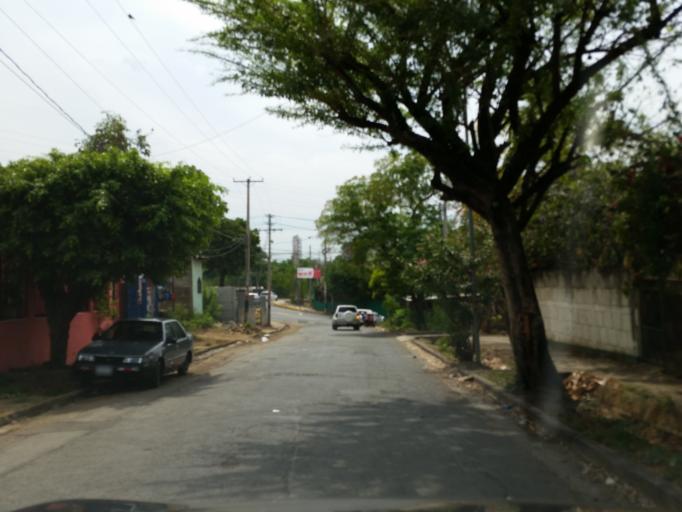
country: NI
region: Managua
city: Managua
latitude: 12.1092
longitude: -86.2505
